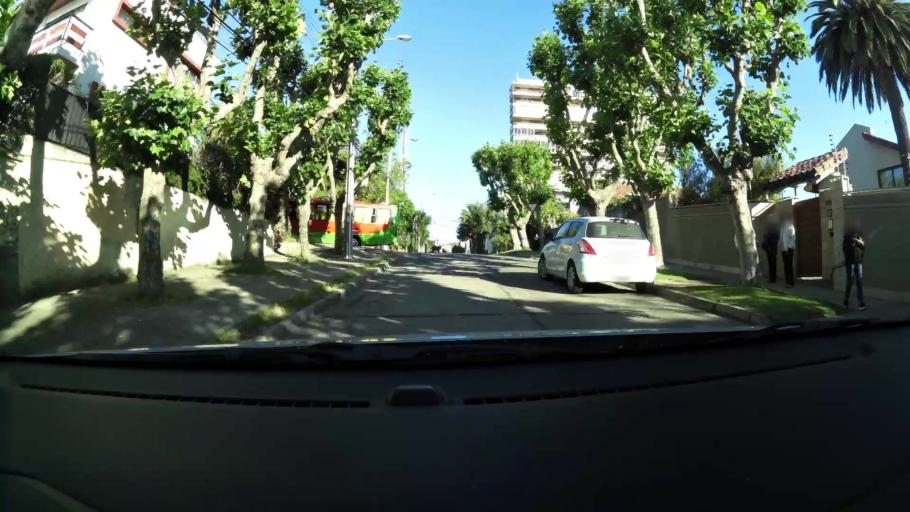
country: CL
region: Valparaiso
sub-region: Provincia de Valparaiso
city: Vina del Mar
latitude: -33.0316
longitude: -71.5821
